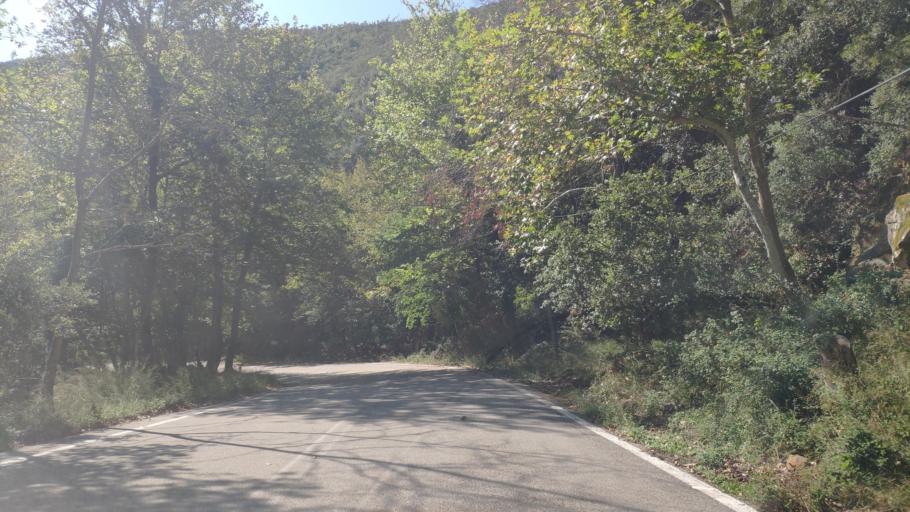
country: GR
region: West Greece
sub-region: Nomos Aitolias kai Akarnanias
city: Sardinia
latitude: 38.9233
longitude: 21.3579
